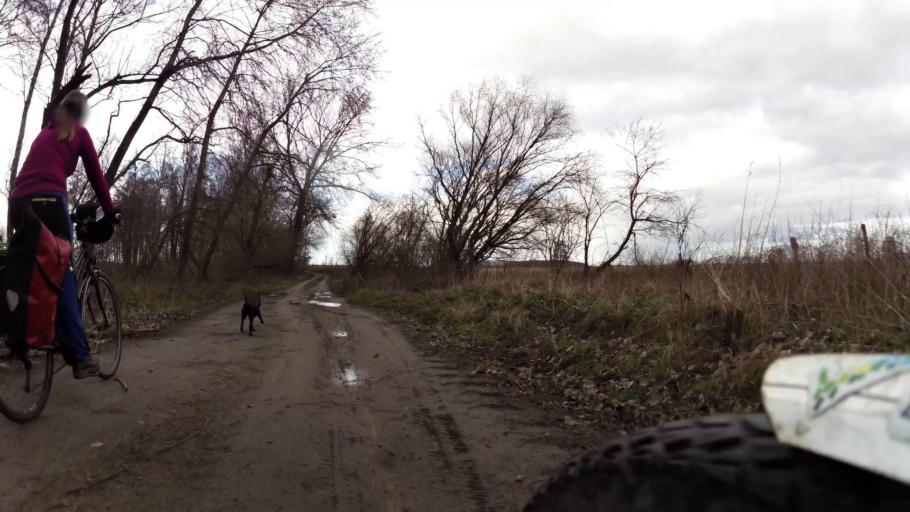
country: PL
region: West Pomeranian Voivodeship
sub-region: Powiat kamienski
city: Kamien Pomorski
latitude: 53.8854
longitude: 14.7187
